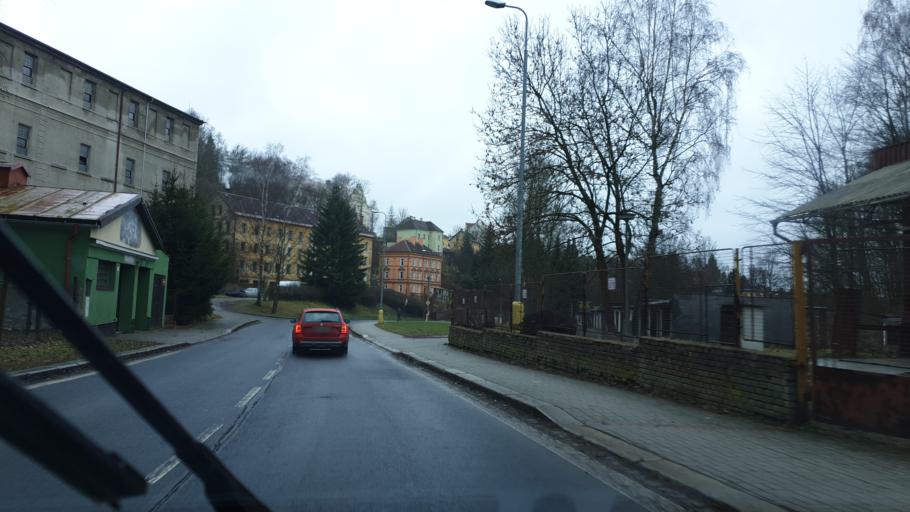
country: CZ
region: Karlovarsky
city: As
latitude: 50.2268
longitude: 12.1869
